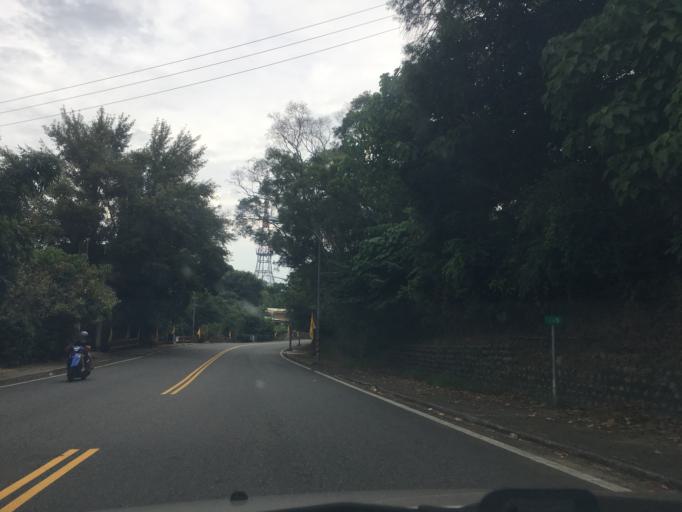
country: TW
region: Taiwan
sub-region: Changhua
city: Chang-hua
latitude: 24.0591
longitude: 120.5718
